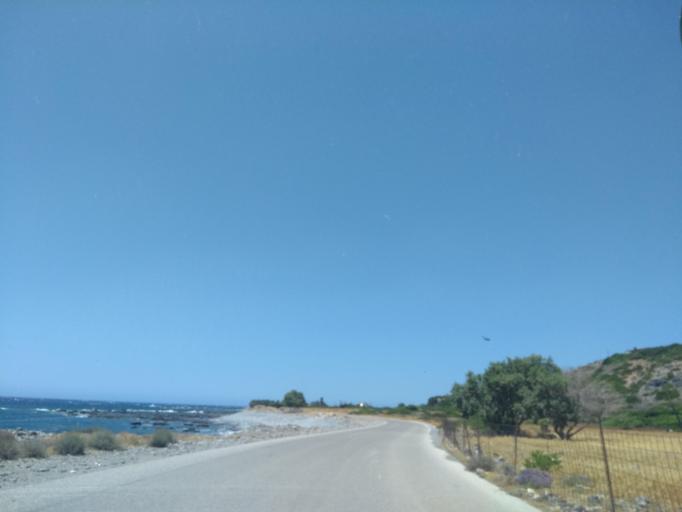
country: GR
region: Crete
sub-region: Nomos Chanias
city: Vryses
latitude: 35.3548
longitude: 23.5332
